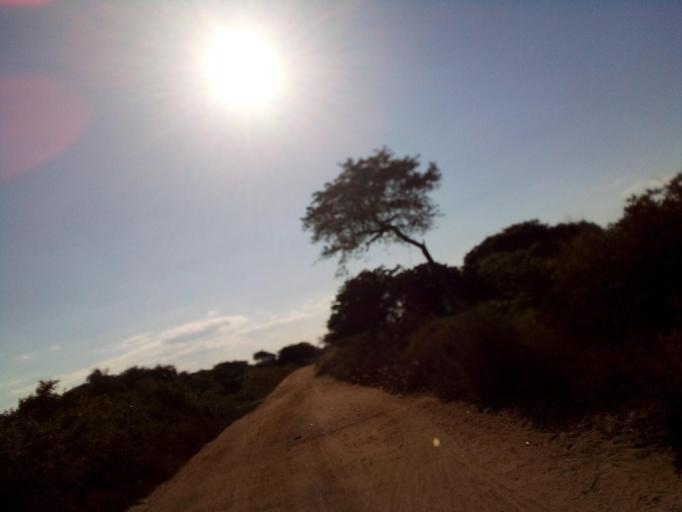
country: MZ
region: Zambezia
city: Quelimane
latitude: -17.4956
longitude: 36.5719
